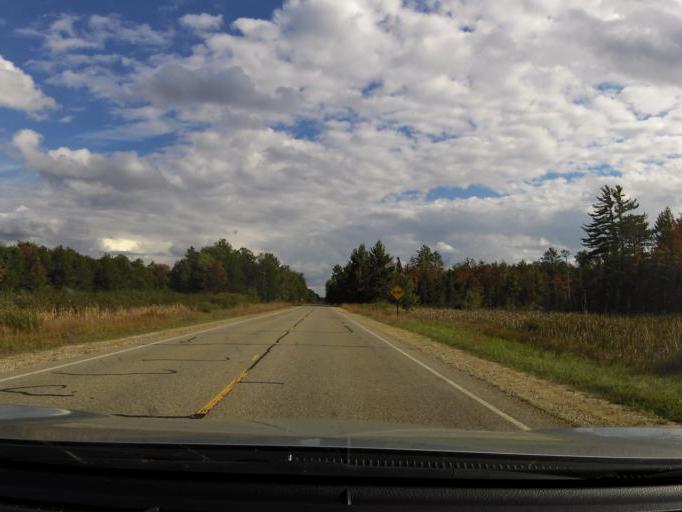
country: US
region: Michigan
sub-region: Roscommon County
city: Roscommon
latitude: 44.4727
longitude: -84.5488
